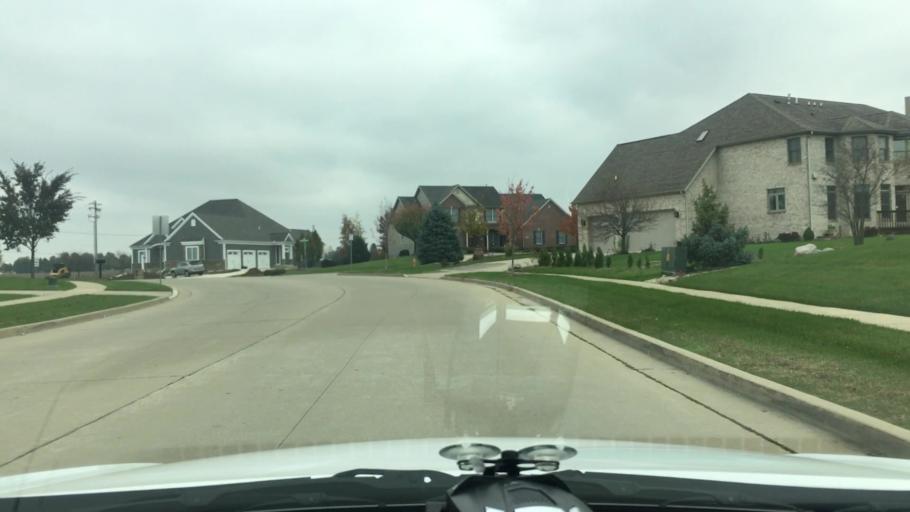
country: US
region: Illinois
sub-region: Champaign County
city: Champaign
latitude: 40.0978
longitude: -88.3205
